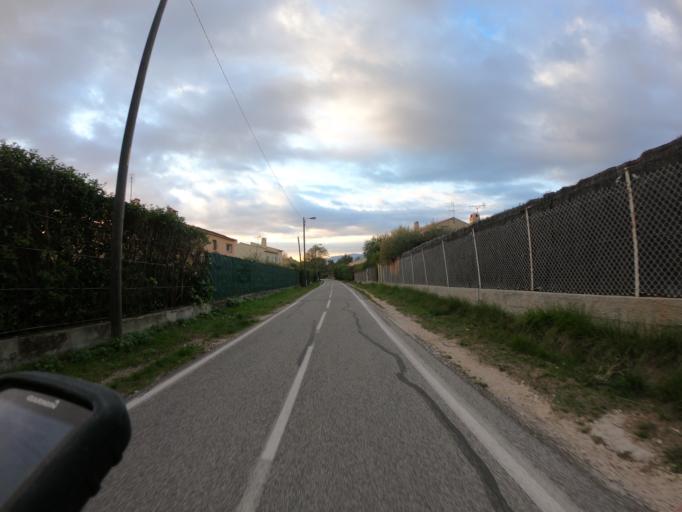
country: FR
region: Provence-Alpes-Cote d'Azur
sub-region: Departement du Var
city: La Garde
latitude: 43.1111
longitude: 5.9955
